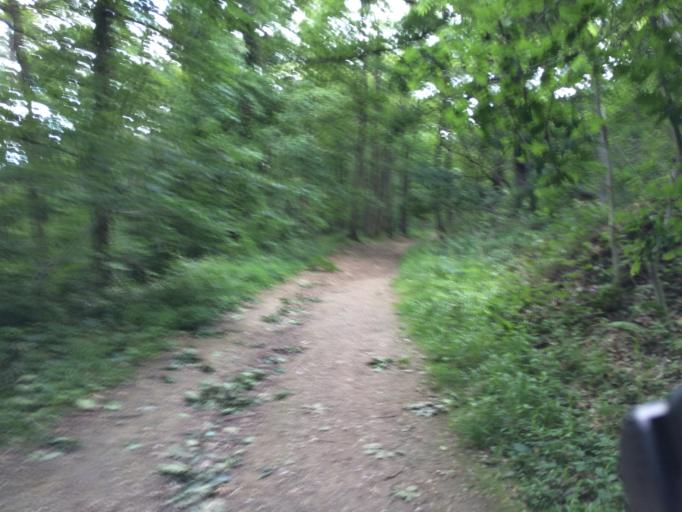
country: FR
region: Ile-de-France
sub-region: Departement de l'Essonne
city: Verrieres-le-Buisson
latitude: 48.7522
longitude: 2.2569
